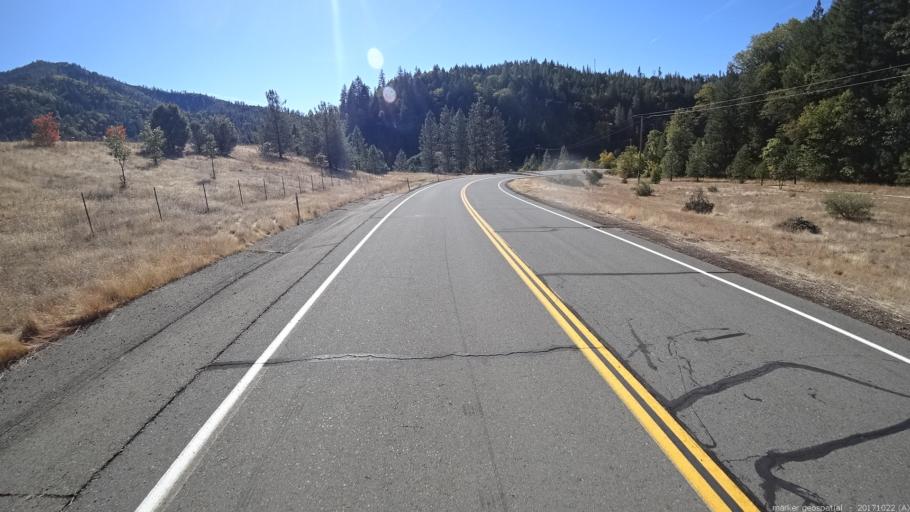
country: US
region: California
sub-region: Siskiyou County
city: Dunsmuir
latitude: 40.9768
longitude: -122.4340
